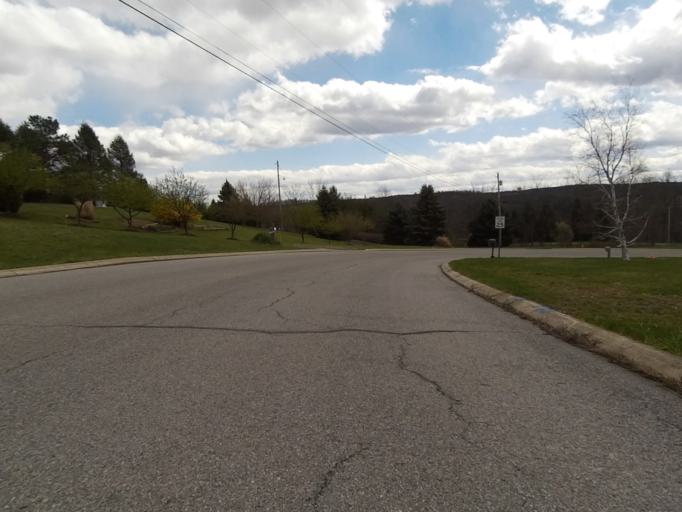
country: US
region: Pennsylvania
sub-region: Centre County
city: Park Forest Village
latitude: 40.8294
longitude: -77.9459
